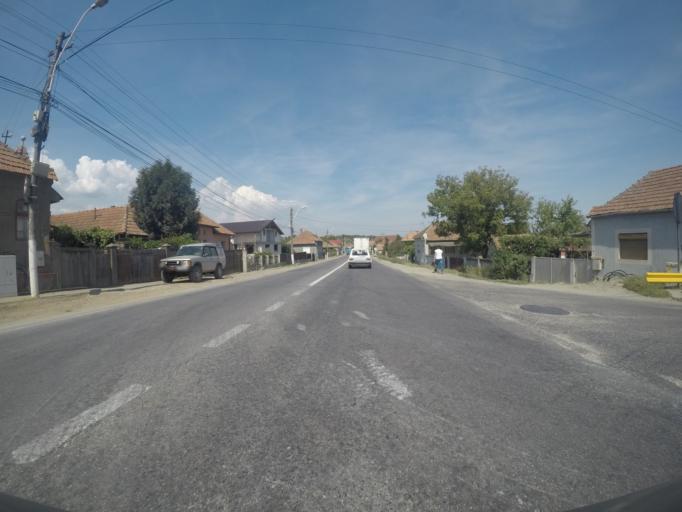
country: RO
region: Alba
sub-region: Oras Teius
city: Teius
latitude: 46.2015
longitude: 23.6714
